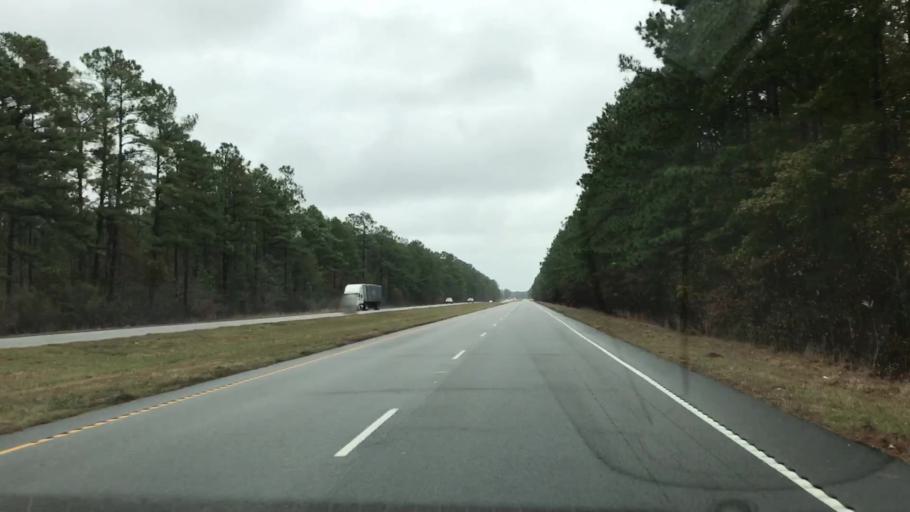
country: US
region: South Carolina
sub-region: Charleston County
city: Awendaw
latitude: 33.1614
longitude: -79.4255
